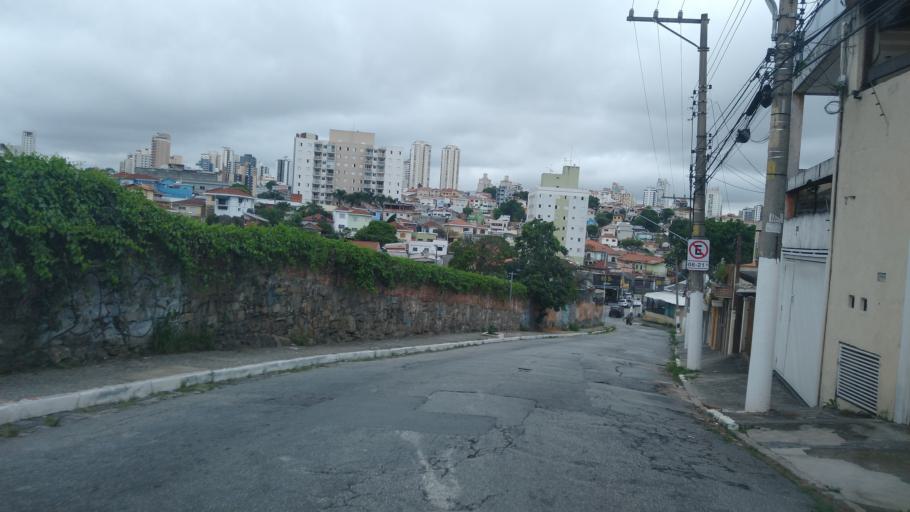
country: BR
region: Sao Paulo
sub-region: Sao Paulo
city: Sao Paulo
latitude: -23.4774
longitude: -46.6224
